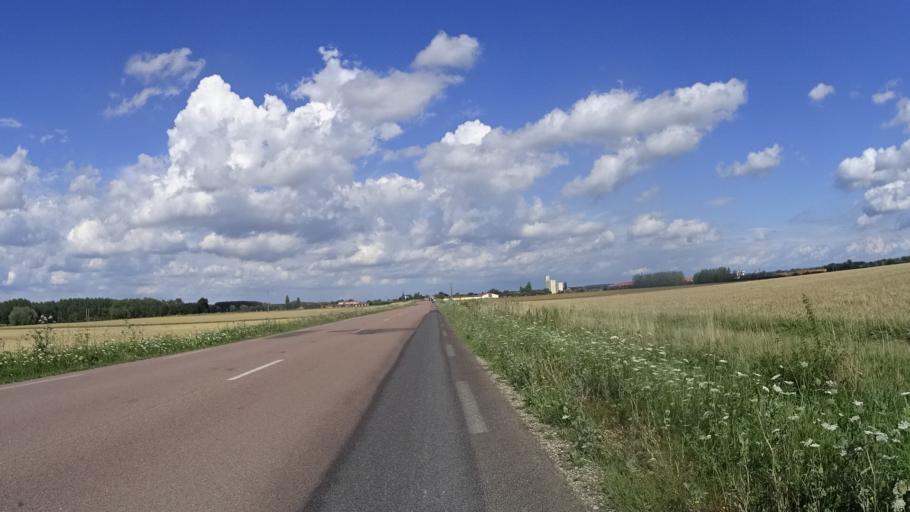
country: FR
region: Champagne-Ardenne
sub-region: Departement de la Marne
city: Pargny-sur-Saulx
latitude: 48.7651
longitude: 4.8187
